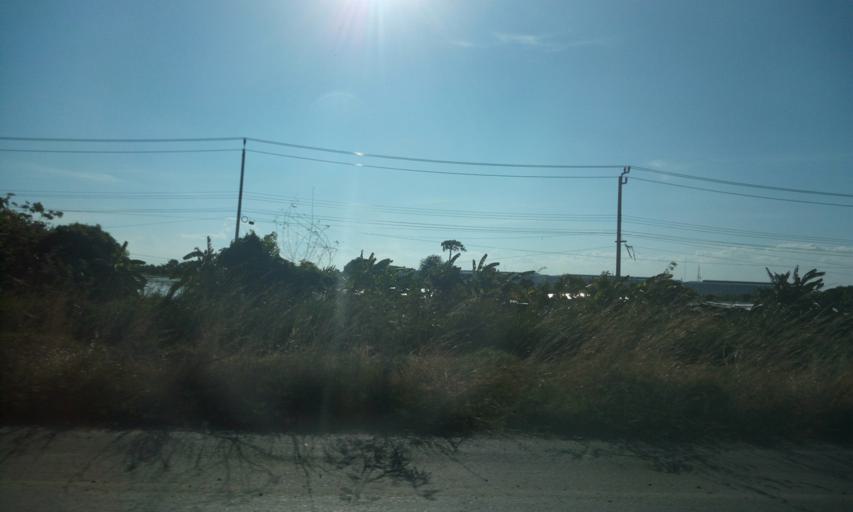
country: TH
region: Samut Prakan
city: Bang Bo District
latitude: 13.5712
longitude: 100.7564
